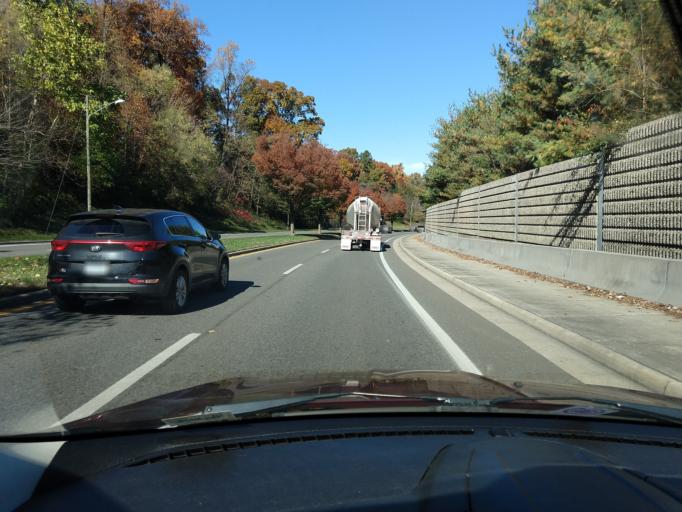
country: US
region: Virginia
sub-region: City of Salem
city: Salem
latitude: 37.2865
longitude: -80.0100
